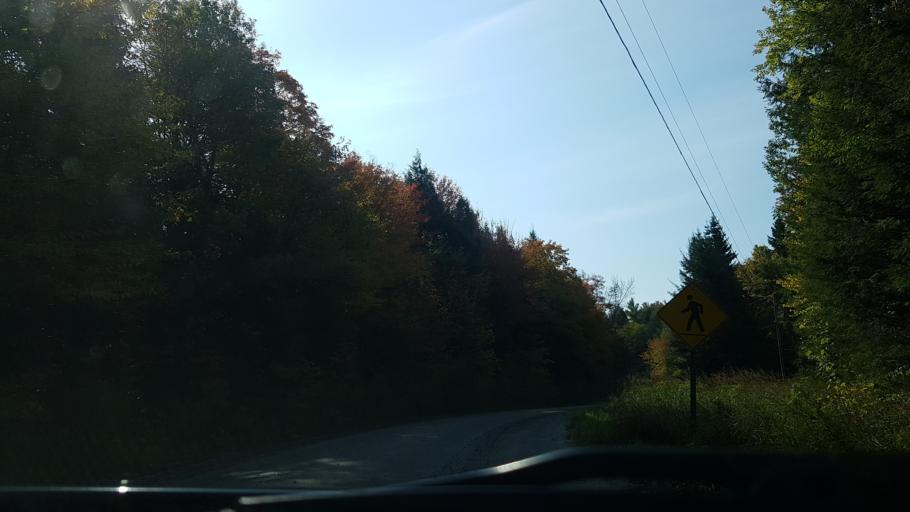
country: CA
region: Ontario
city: Bracebridge
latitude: 44.9370
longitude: -79.2379
